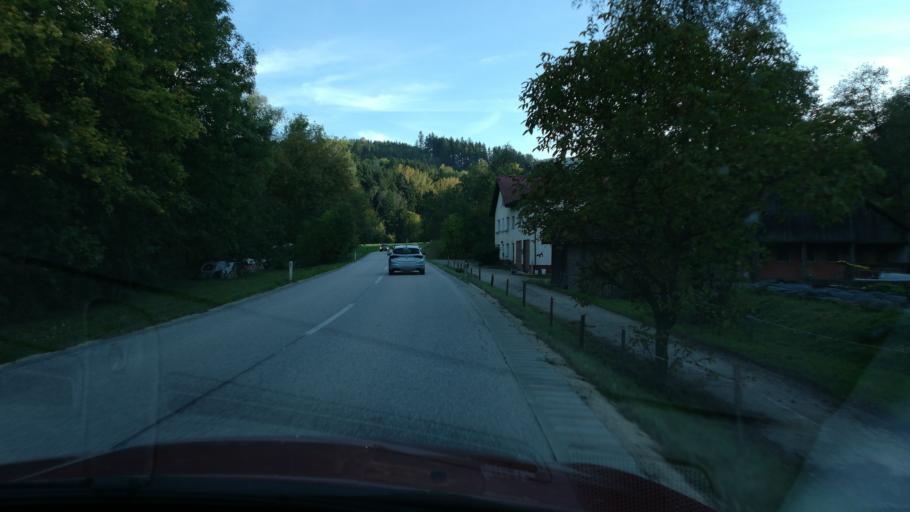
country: AT
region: Upper Austria
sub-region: Politischer Bezirk Steyr-Land
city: Ternberg
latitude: 47.9710
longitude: 14.3324
